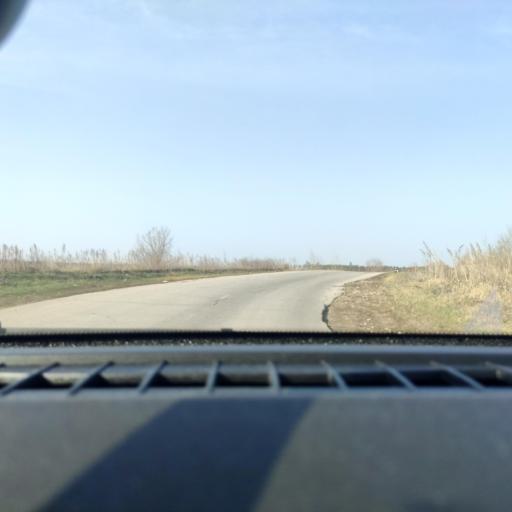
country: RU
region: Samara
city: Tol'yatti
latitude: 53.4871
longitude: 49.3489
